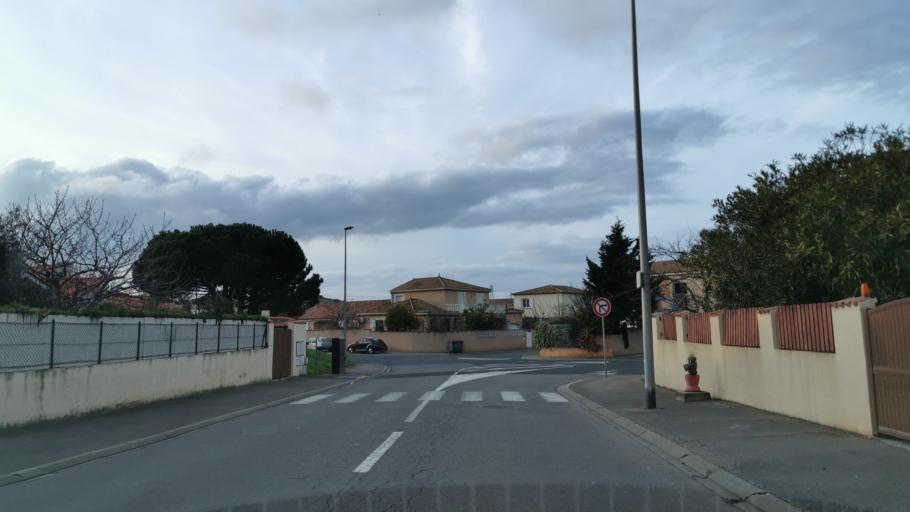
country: FR
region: Languedoc-Roussillon
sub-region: Departement de l'Aude
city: Narbonne
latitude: 43.1880
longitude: 2.9790
